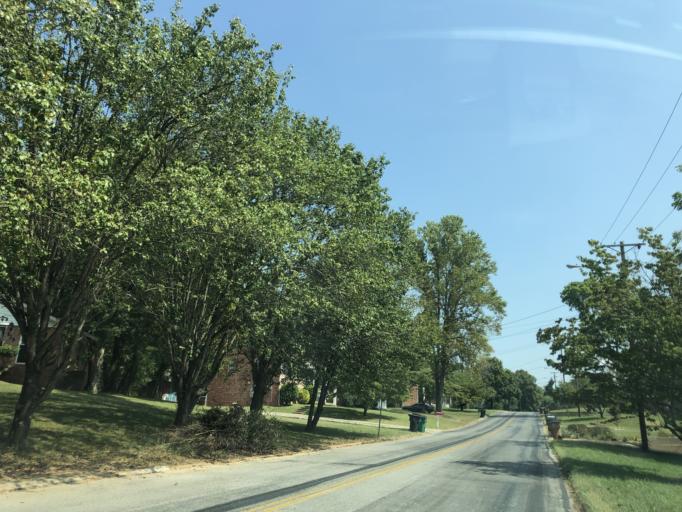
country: US
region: Tennessee
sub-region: Davidson County
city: Lakewood
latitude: 36.1548
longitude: -86.6446
